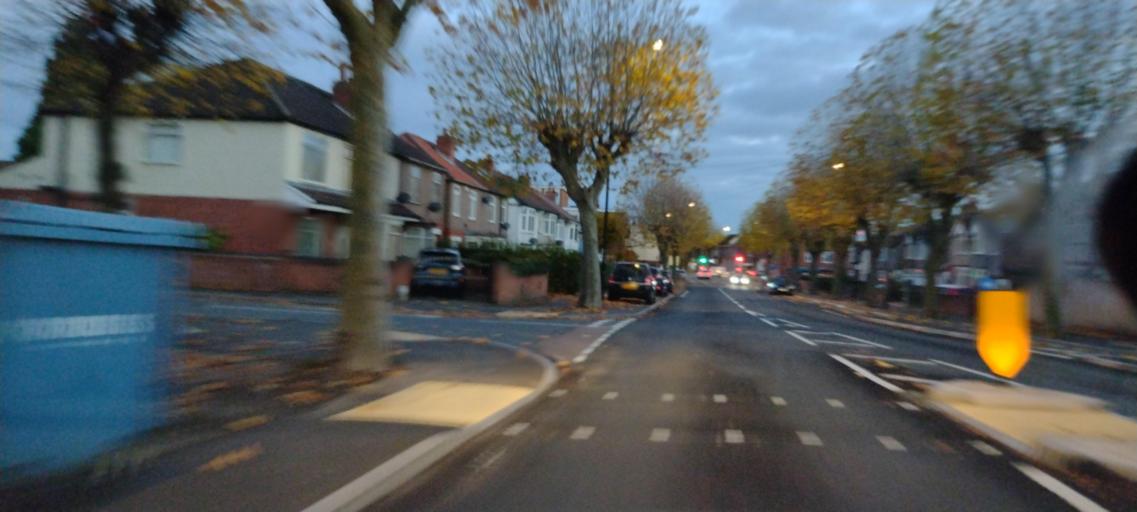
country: GB
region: England
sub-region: Coventry
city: Coventry
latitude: 52.4182
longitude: -1.5284
